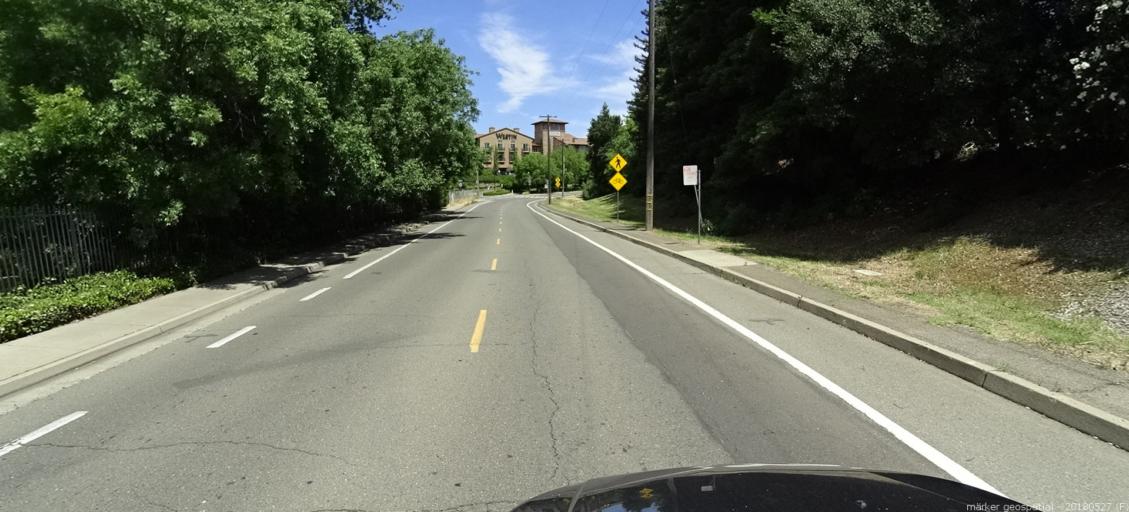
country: US
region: California
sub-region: Yolo County
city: West Sacramento
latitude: 38.5325
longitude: -121.5180
